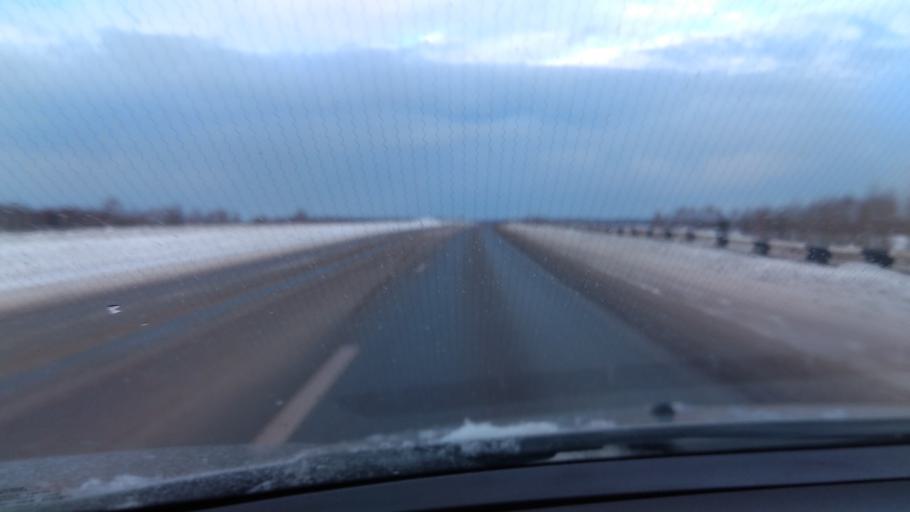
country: RU
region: Sverdlovsk
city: Nev'yansk
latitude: 57.5033
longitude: 60.1736
